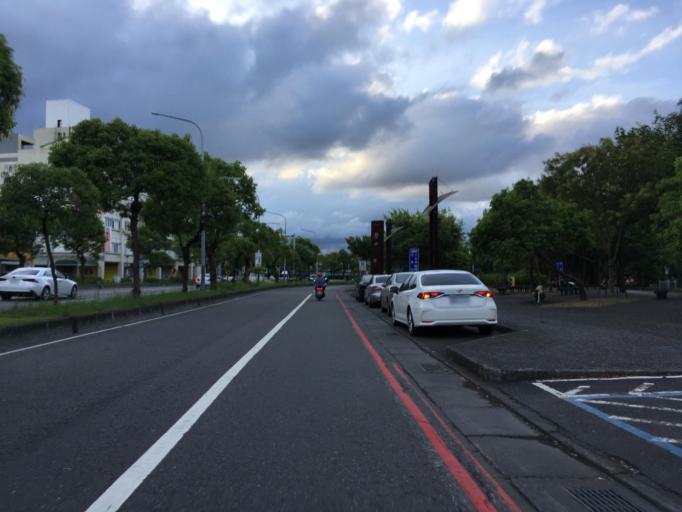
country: TW
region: Taiwan
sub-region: Yilan
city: Yilan
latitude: 24.6702
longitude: 121.7650
